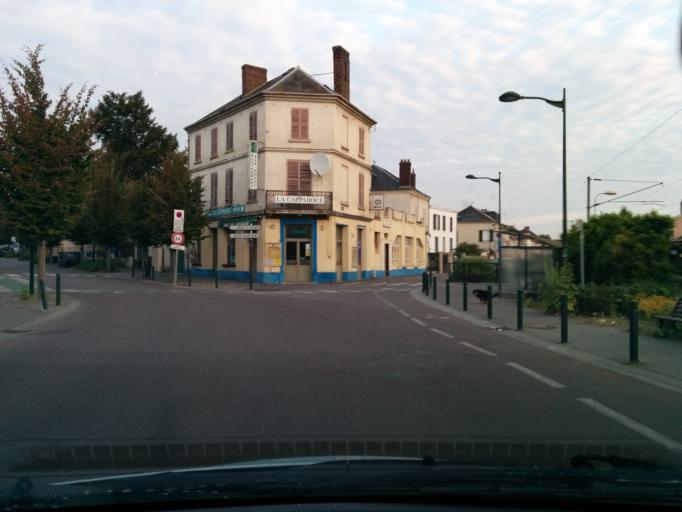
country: FR
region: Haute-Normandie
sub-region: Departement de l'Eure
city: Vernon
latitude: 49.0905
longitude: 1.4794
